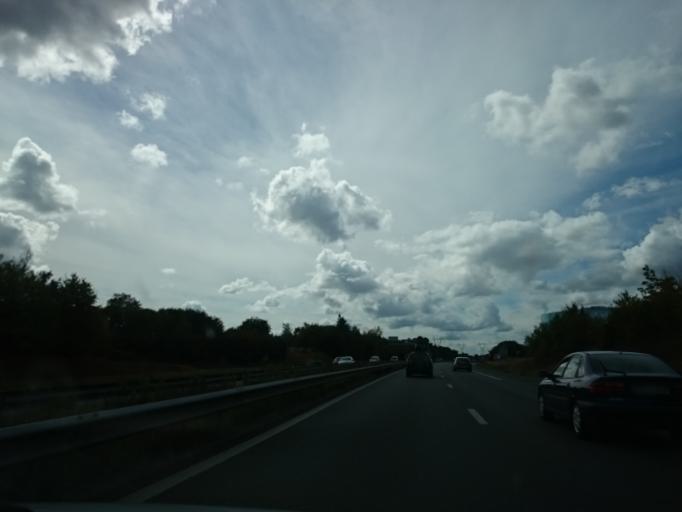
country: FR
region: Pays de la Loire
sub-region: Departement de la Loire-Atlantique
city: Les Sorinieres
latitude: 47.1592
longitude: -1.5427
